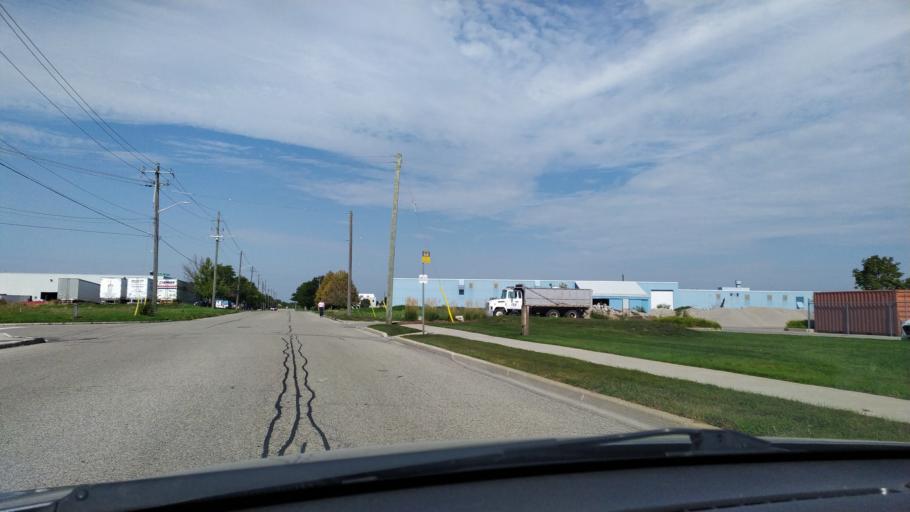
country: CA
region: Ontario
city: Waterloo
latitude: 43.5087
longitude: -80.5283
